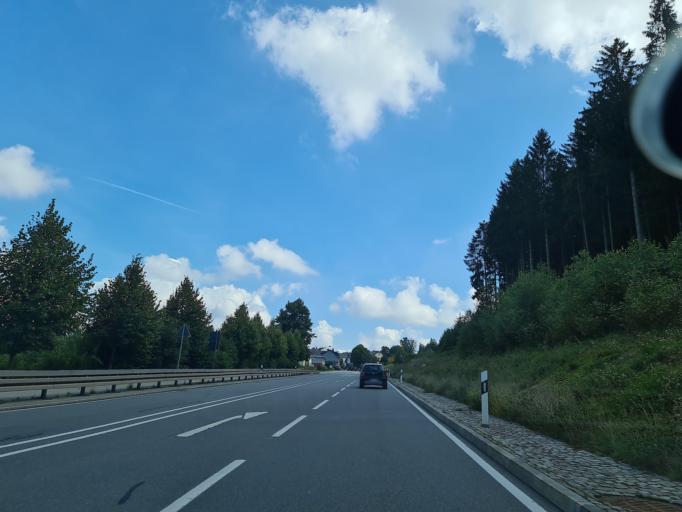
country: DE
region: Saxony
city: Zoblitz
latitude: 50.6599
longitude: 13.2185
